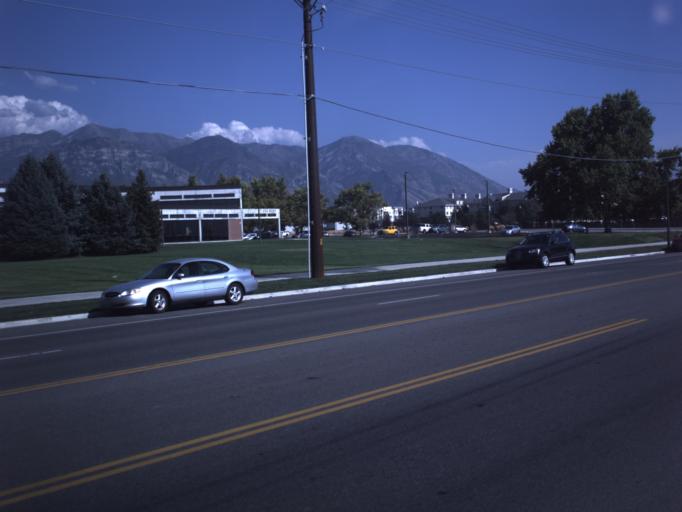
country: US
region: Utah
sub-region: Utah County
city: Orem
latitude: 40.2802
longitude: -111.7310
